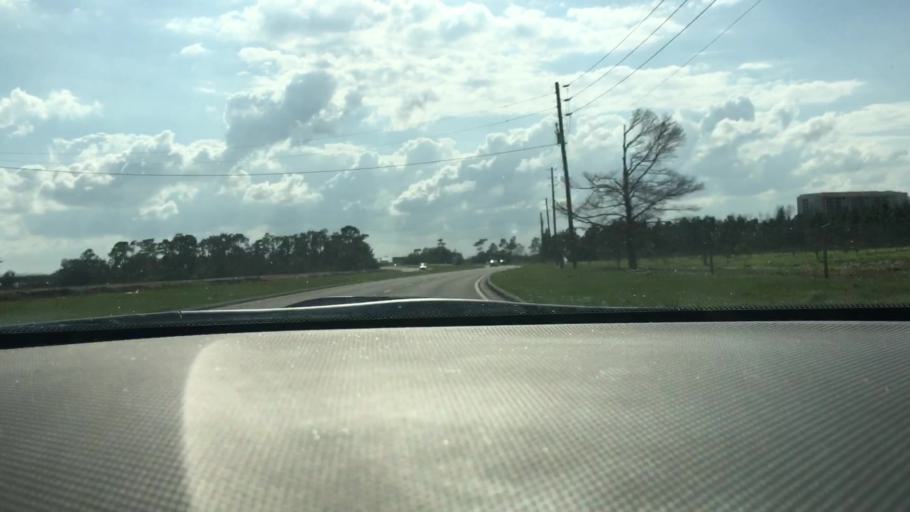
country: US
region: Florida
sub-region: Orange County
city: Williamsburg
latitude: 28.4023
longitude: -81.4854
